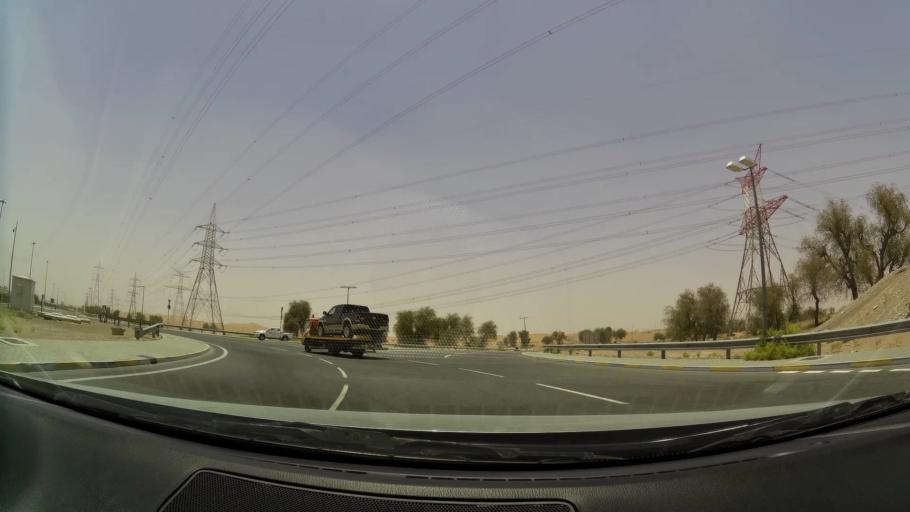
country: OM
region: Al Buraimi
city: Al Buraymi
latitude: 24.2749
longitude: 55.7198
